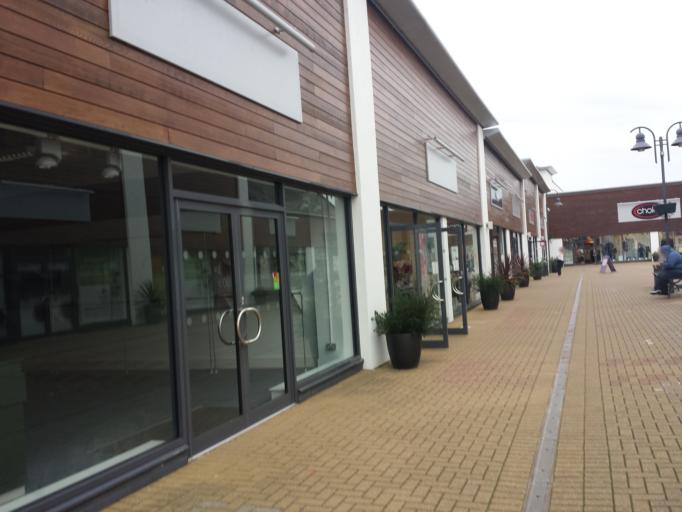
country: GB
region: England
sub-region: Essex
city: Little Clacton
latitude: 51.8185
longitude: 1.1675
